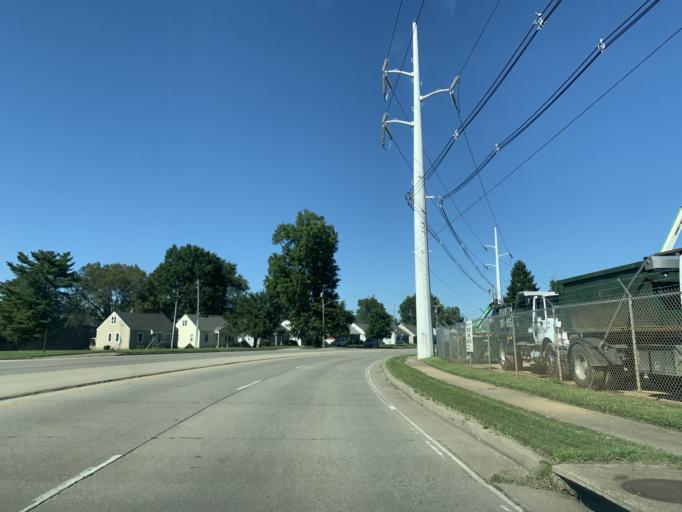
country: US
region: Kentucky
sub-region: Jefferson County
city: West Buechel
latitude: 38.1948
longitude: -85.6656
